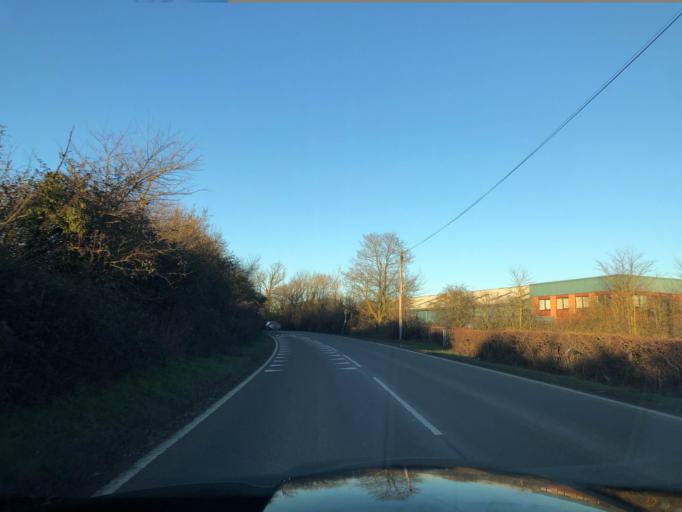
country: GB
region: England
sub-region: Warwickshire
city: Harbury
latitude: 52.2073
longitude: -1.4404
